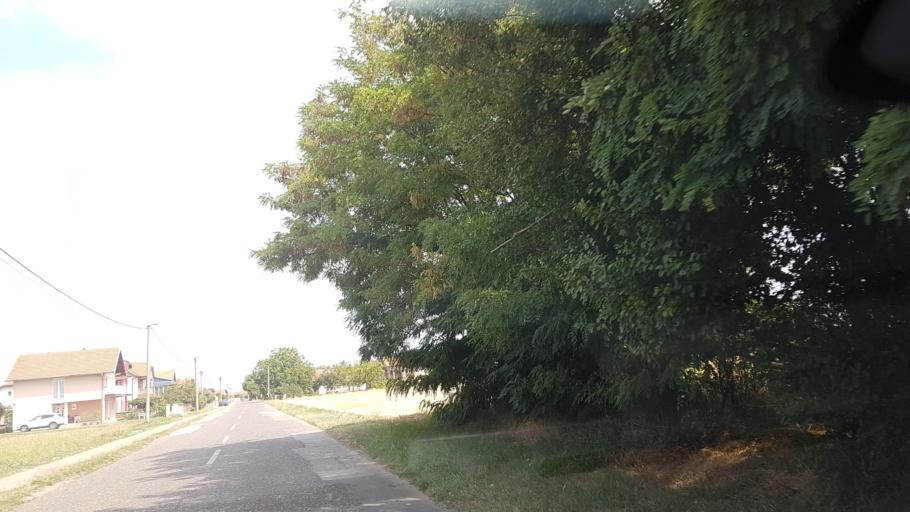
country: BA
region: Republika Srpska
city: Bijeljina
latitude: 44.7830
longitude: 19.2233
